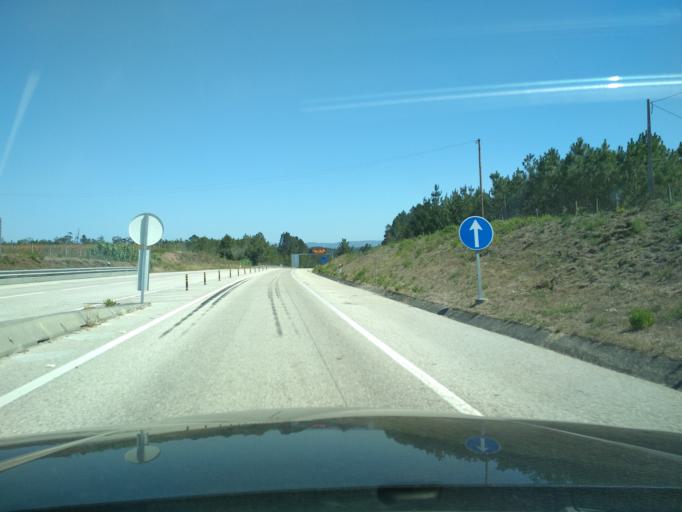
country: PT
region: Leiria
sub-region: Pombal
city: Lourical
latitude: 39.9889
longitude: -8.7805
